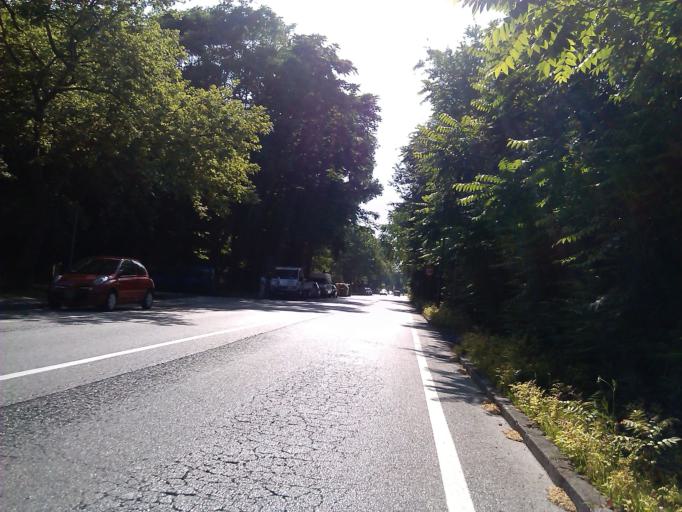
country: IT
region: Veneto
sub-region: Provincia di Venezia
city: Campalto
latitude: 45.4820
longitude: 12.2901
